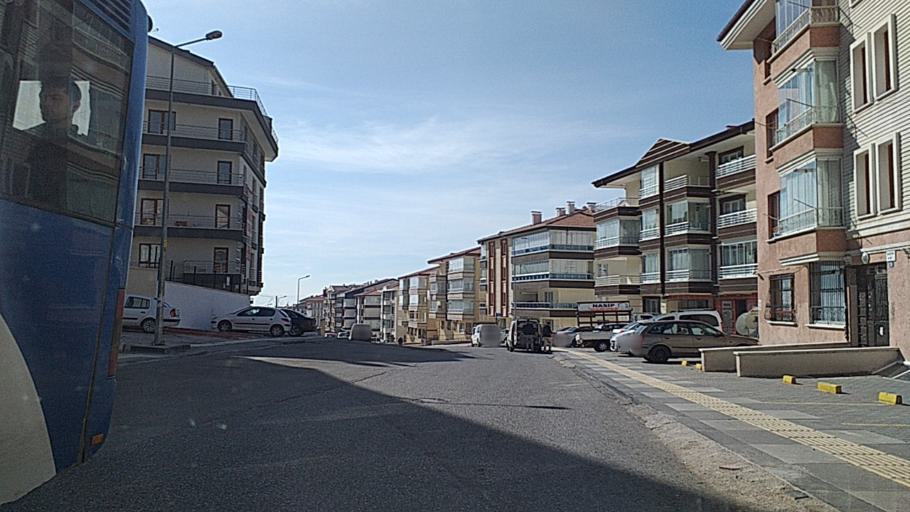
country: TR
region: Ankara
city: Ankara
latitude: 39.9925
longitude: 32.8116
